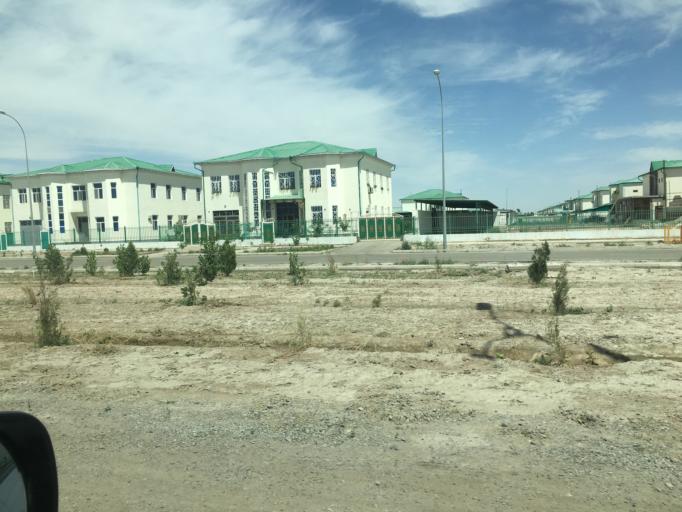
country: TM
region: Dasoguz
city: Dasoguz
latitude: 41.8158
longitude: 59.9519
